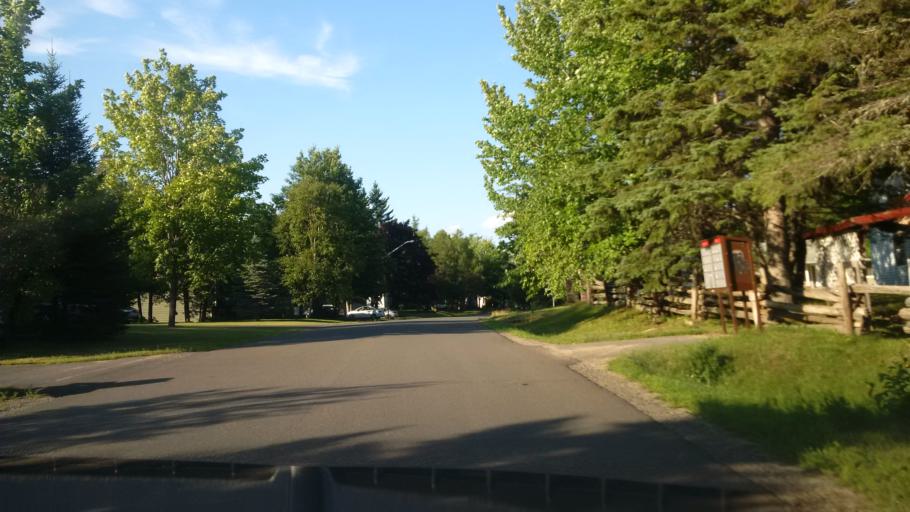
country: CA
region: New Brunswick
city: Fredericton
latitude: 45.8917
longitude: -66.6917
